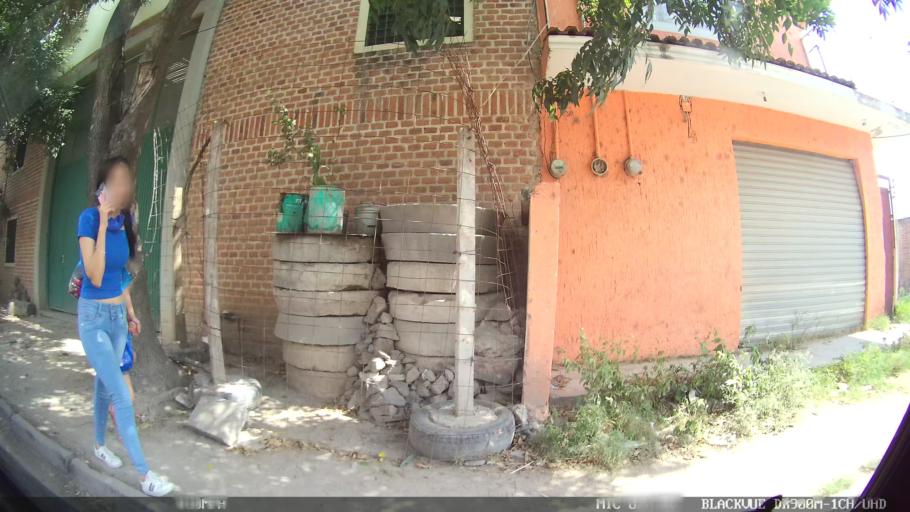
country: MX
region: Jalisco
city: Tonala
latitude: 20.6686
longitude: -103.2371
